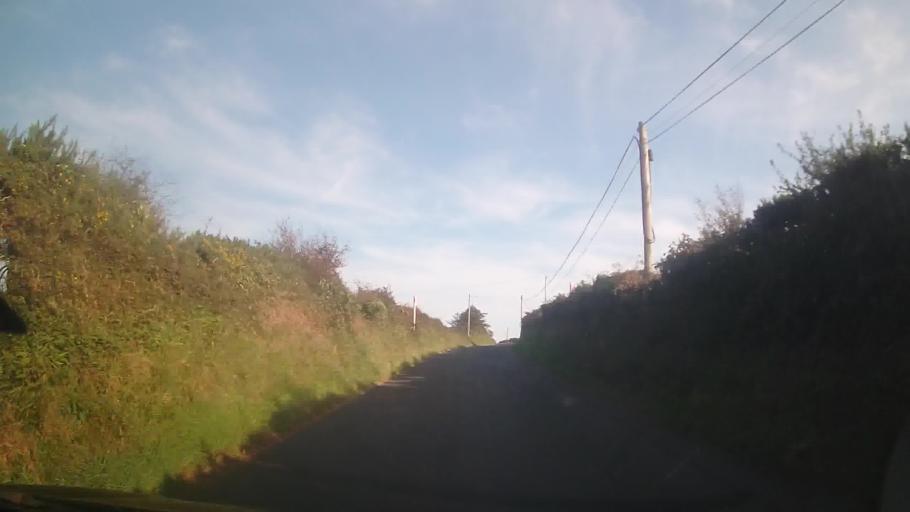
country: GB
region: Wales
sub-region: Pembrokeshire
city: Fishguard
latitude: 51.9900
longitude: -4.9641
